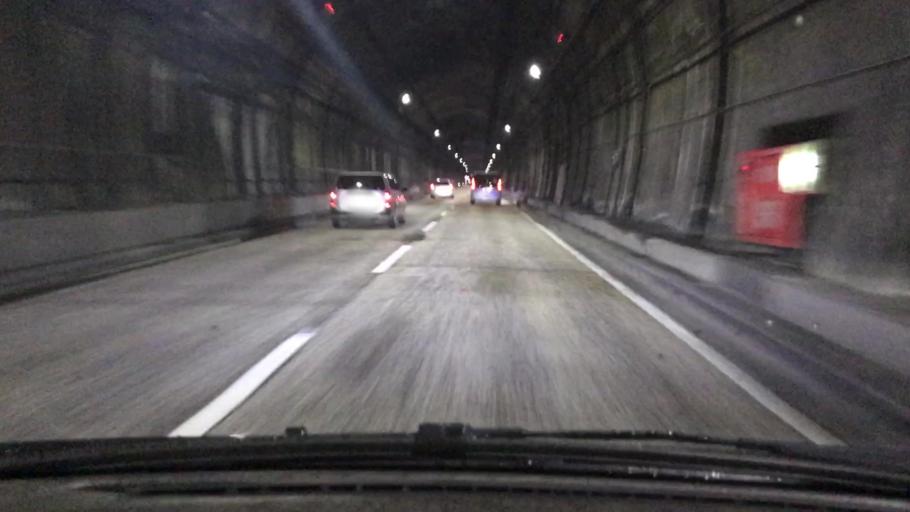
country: JP
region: Hyogo
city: Kobe
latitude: 34.7457
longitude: 135.1691
